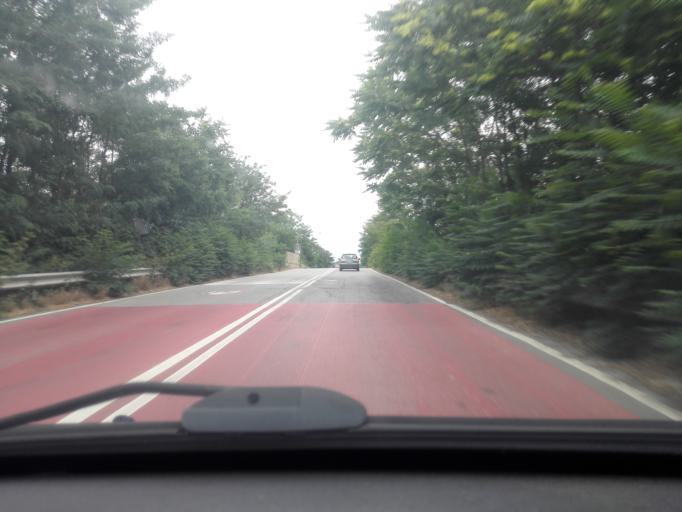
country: IT
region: Piedmont
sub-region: Provincia di Alessandria
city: Pozzolo Formigaro
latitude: 44.7910
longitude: 8.7787
